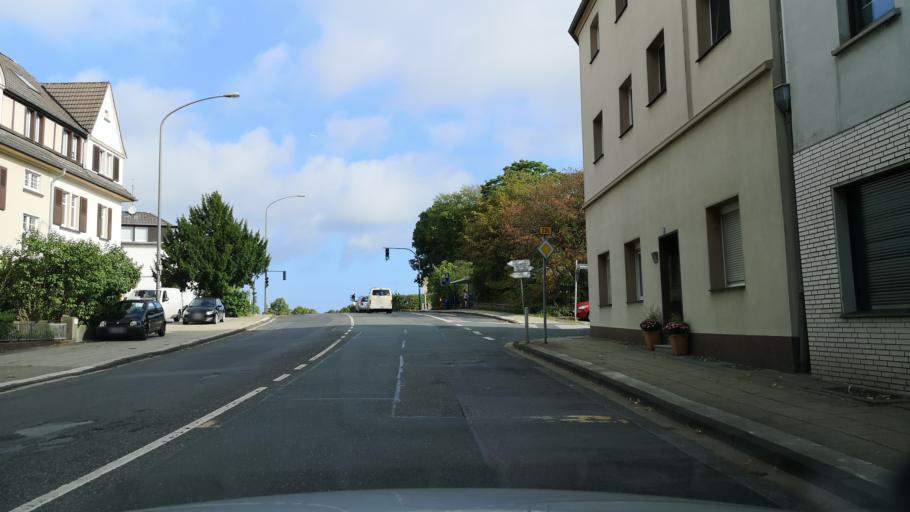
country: DE
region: North Rhine-Westphalia
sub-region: Regierungsbezirk Dusseldorf
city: Velbert
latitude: 51.3728
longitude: 7.0167
